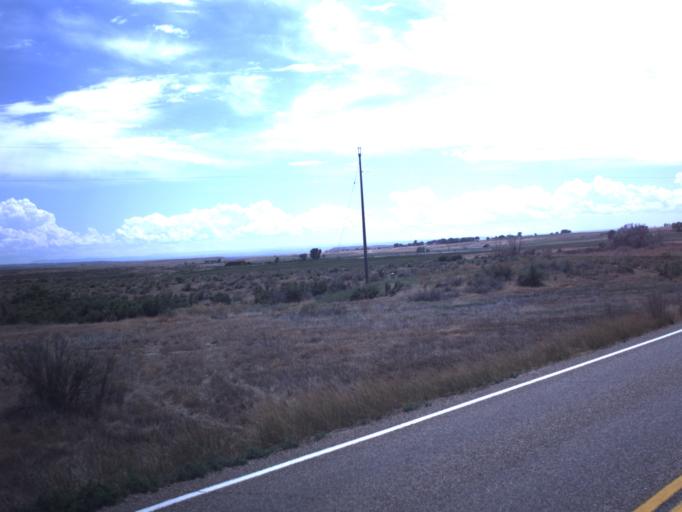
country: US
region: Utah
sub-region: Uintah County
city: Maeser
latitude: 40.2559
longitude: -109.6845
